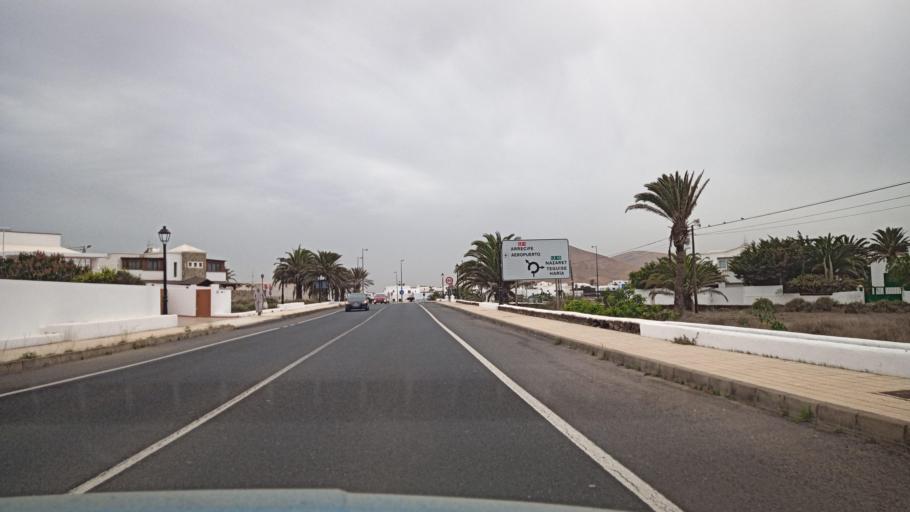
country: ES
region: Canary Islands
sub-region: Provincia de Las Palmas
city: Nazaret
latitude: 29.0149
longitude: -13.5443
